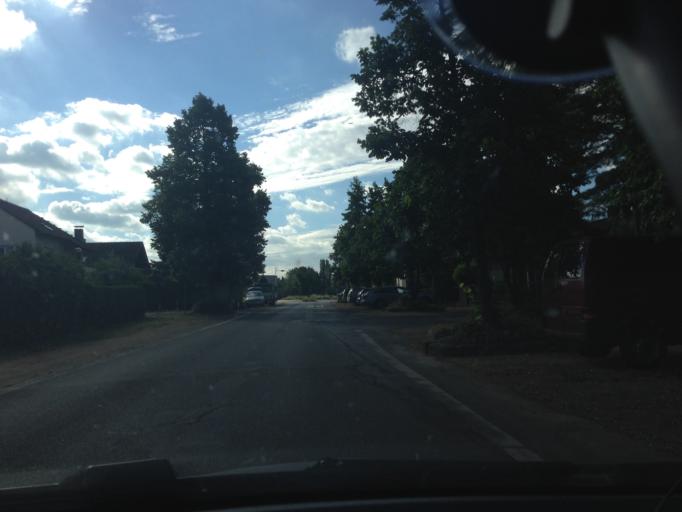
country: DE
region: Hesse
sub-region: Regierungsbezirk Darmstadt
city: Offenbach
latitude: 50.1165
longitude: 8.7888
